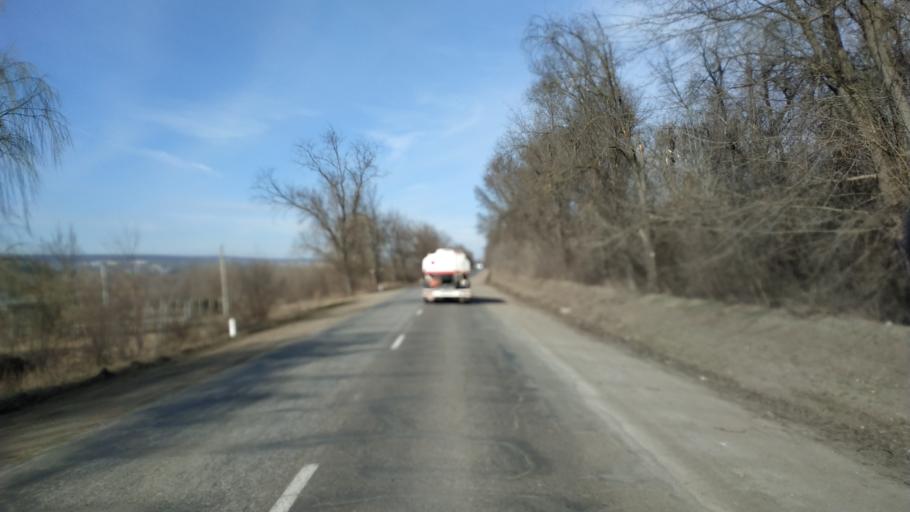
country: MD
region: Laloveni
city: Ialoveni
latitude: 46.9535
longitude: 28.7589
